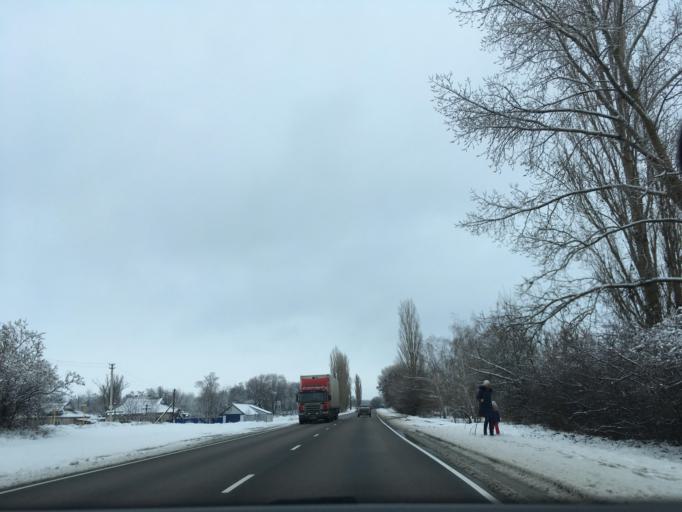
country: RU
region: Voronezj
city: Zabolotovka
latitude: 50.2471
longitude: 39.3639
